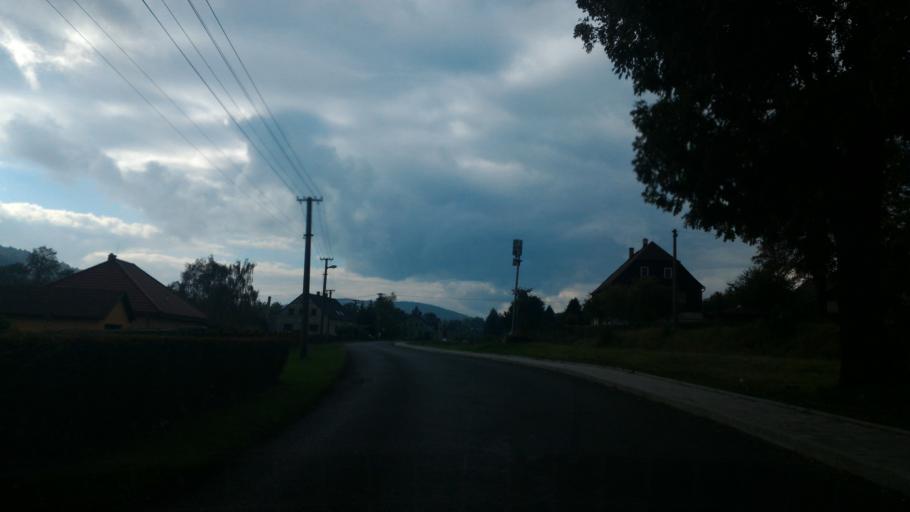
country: CZ
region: Ustecky
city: Dolni Podluzi
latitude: 50.8830
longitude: 14.5675
